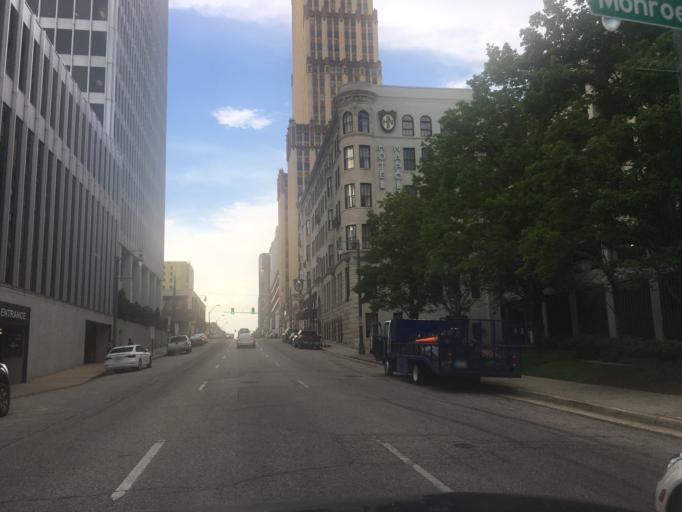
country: US
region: Tennessee
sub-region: Shelby County
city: Memphis
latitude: 35.1435
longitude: -90.0507
